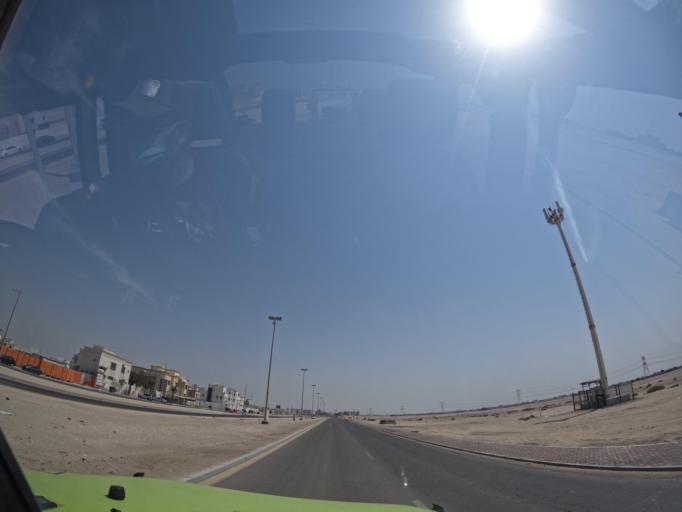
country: AE
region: Abu Dhabi
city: Abu Dhabi
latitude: 24.3048
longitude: 54.5444
